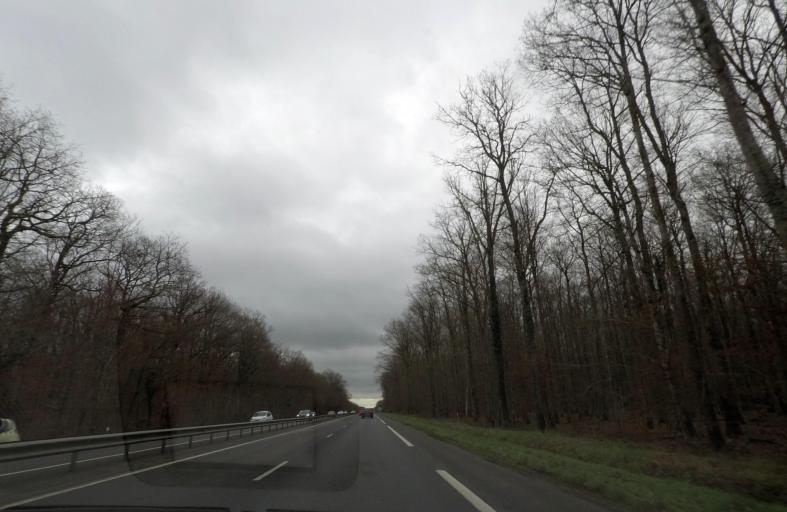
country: FR
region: Centre
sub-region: Departement du Loir-et-Cher
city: Cellettes
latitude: 47.5478
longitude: 1.3942
